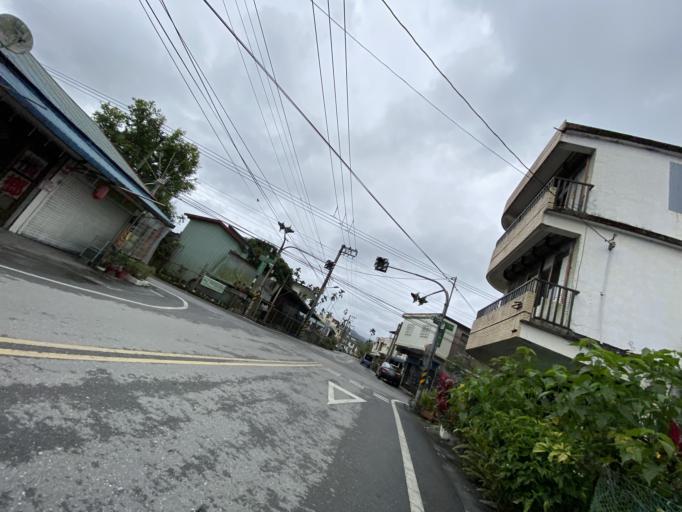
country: TW
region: Taiwan
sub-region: Hualien
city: Hualian
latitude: 23.6565
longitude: 121.4518
